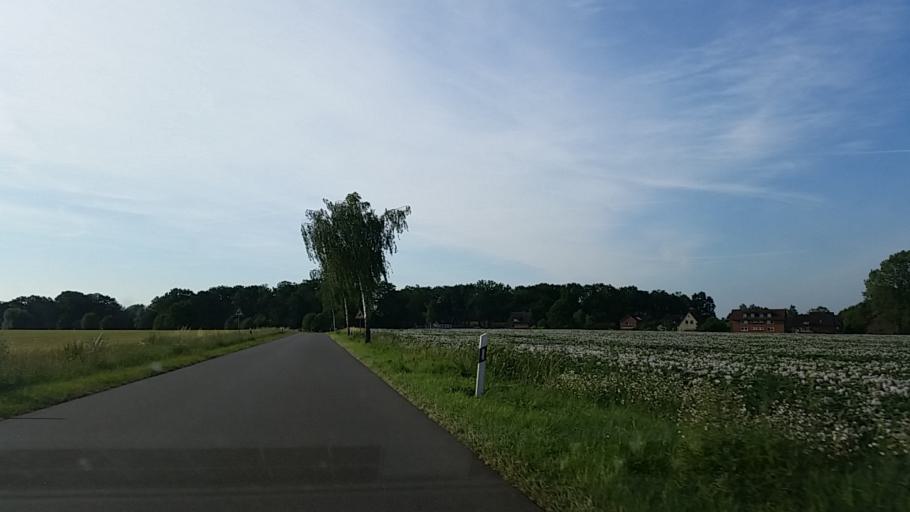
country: DE
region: Lower Saxony
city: Wieren
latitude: 52.9144
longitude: 10.6572
